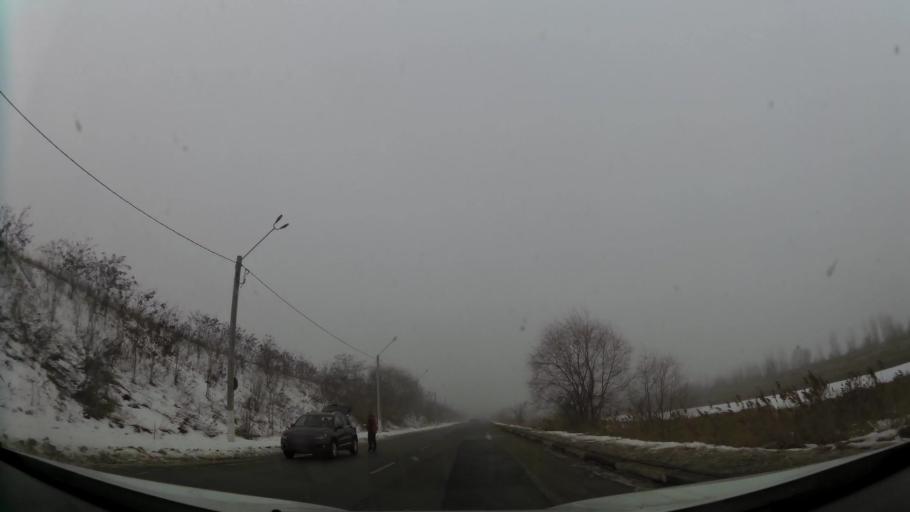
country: RO
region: Ilfov
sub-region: Comuna Chiajna
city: Chiajna
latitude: 44.4647
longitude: 25.9872
